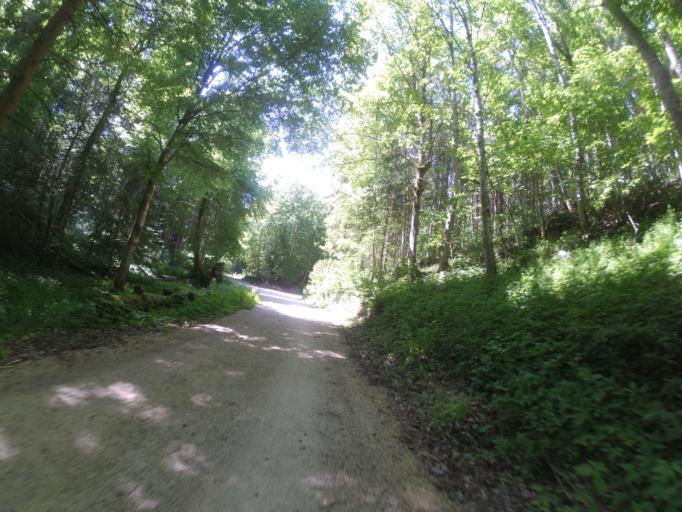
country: DE
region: Baden-Wuerttemberg
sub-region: Tuebingen Region
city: Berghulen
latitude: 48.4844
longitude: 9.8024
